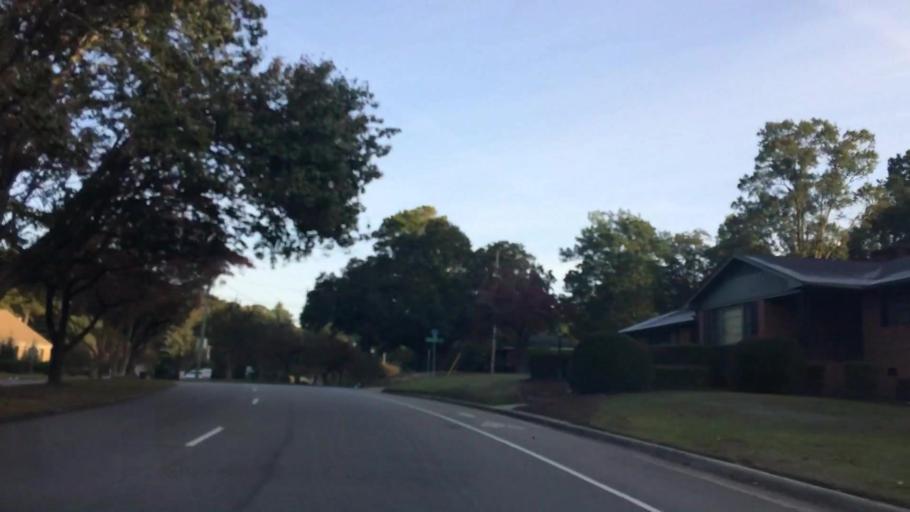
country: US
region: North Carolina
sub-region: Pitt County
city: Greenville
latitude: 35.5906
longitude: -77.3604
